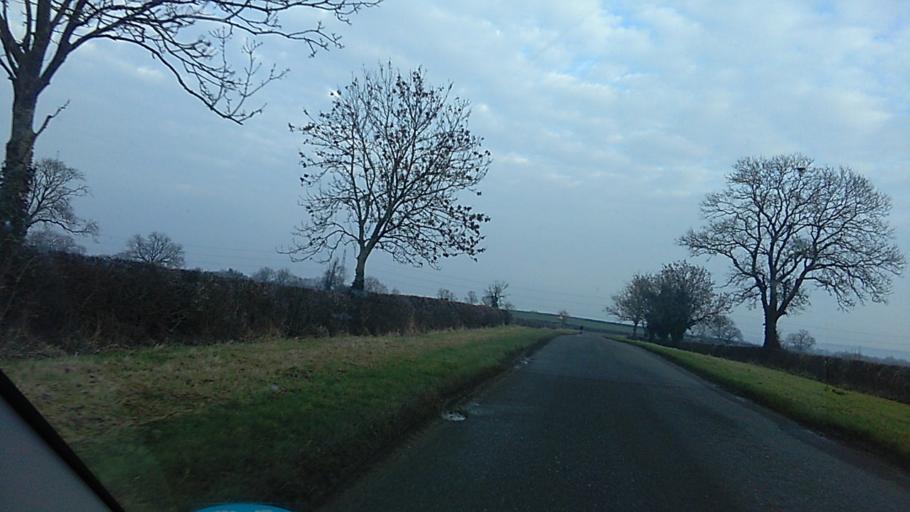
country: GB
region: England
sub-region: Nottinghamshire
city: Cropwell Bishop
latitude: 52.8538
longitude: -0.9675
